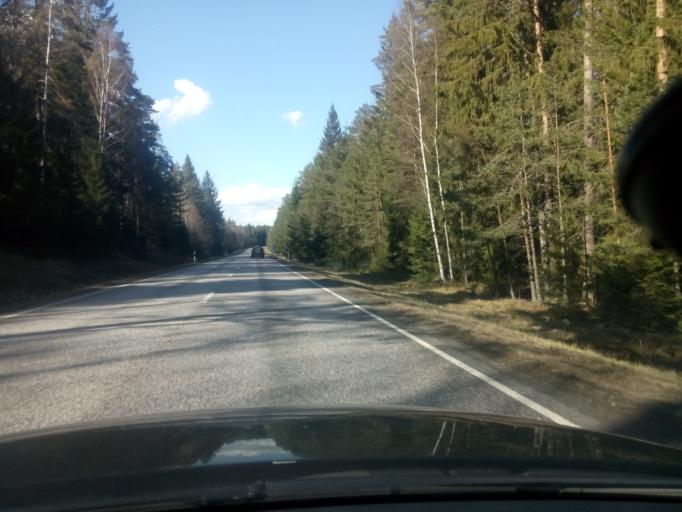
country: SE
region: Soedermanland
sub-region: Flens Kommun
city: Malmkoping
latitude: 59.1973
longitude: 16.7887
